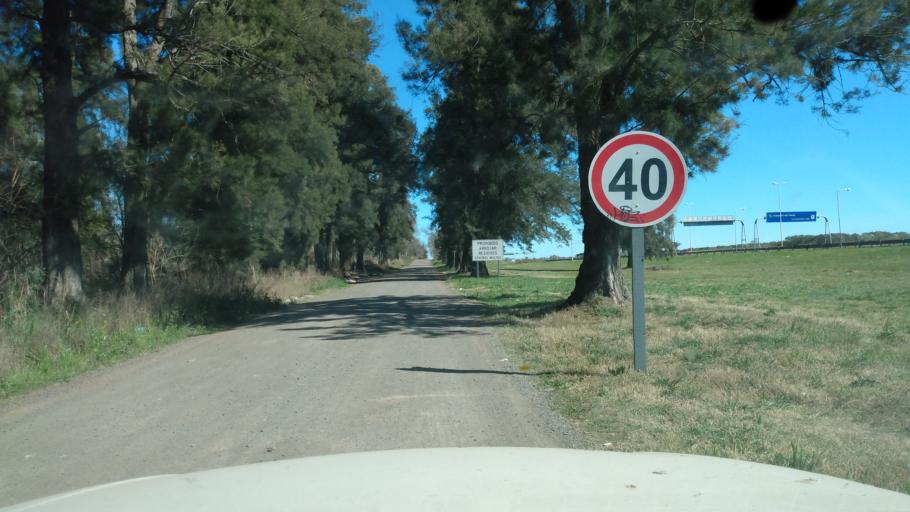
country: AR
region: Buenos Aires
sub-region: Partido de Lujan
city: Lujan
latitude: -34.5680
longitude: -59.0663
